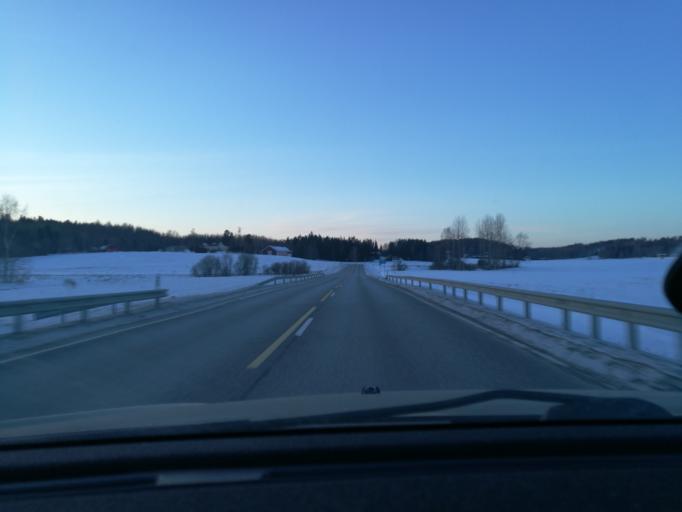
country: FI
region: Uusimaa
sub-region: Helsinki
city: Vihti
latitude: 60.4314
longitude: 24.4246
